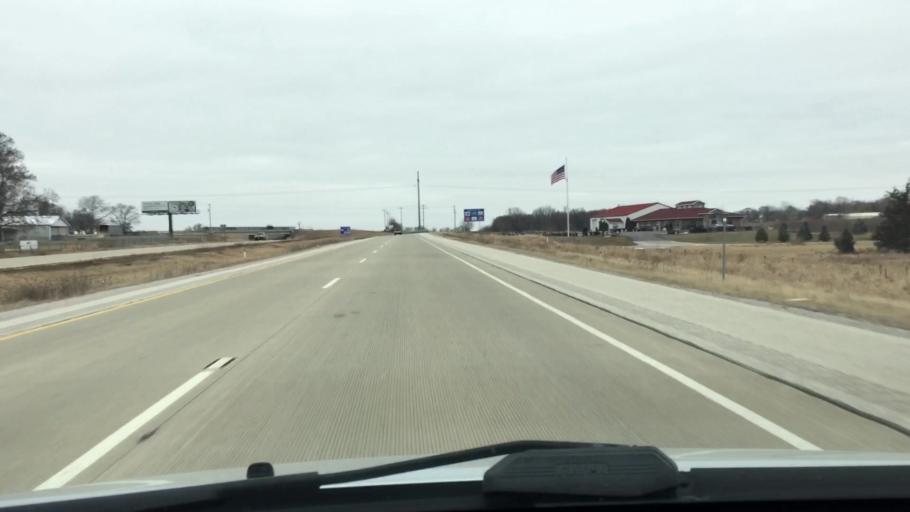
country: US
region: Wisconsin
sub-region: Jefferson County
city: Watertown
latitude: 43.1464
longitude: -88.7348
